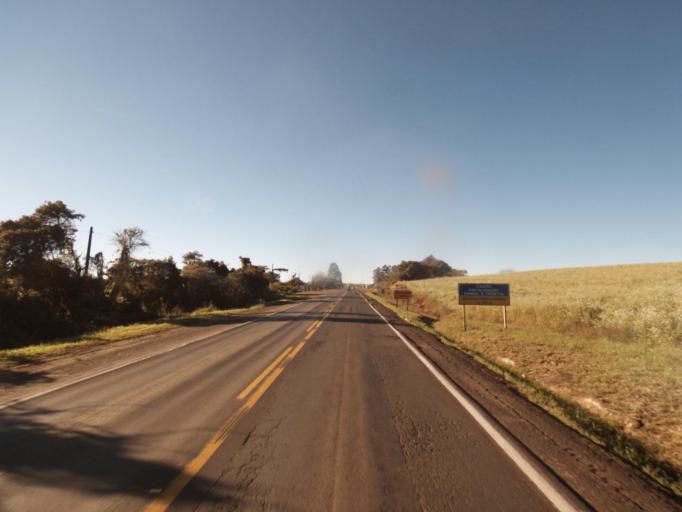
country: AR
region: Misiones
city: Bernardo de Irigoyen
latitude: -26.3156
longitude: -53.5488
